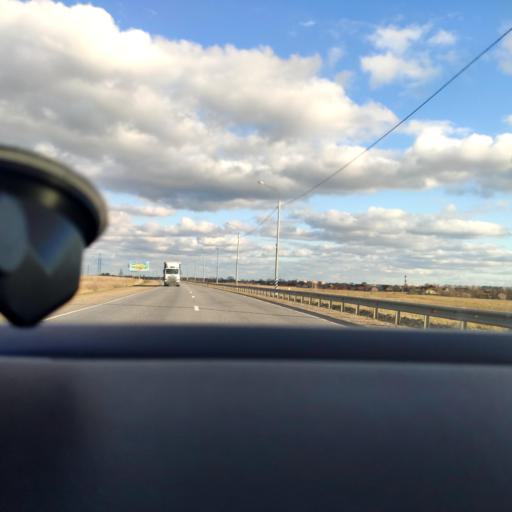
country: RU
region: Moskovskaya
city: Yegor'yevsk
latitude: 55.4007
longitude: 39.0601
